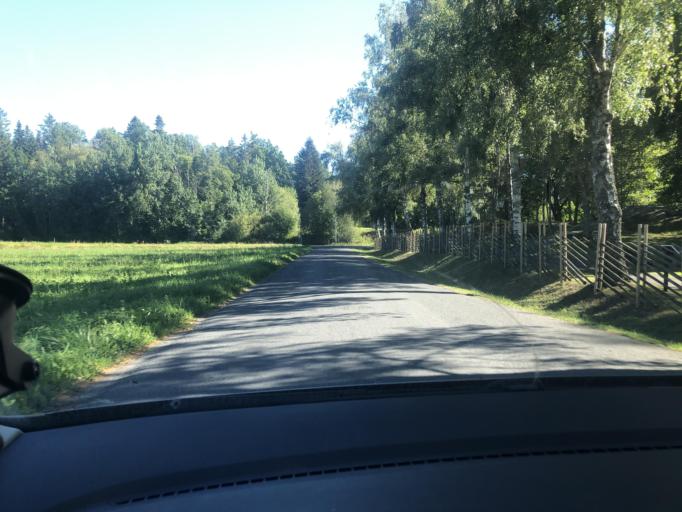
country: SE
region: Joenkoeping
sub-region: Jonkopings Kommun
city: Huskvarna
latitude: 57.7972
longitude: 14.3132
